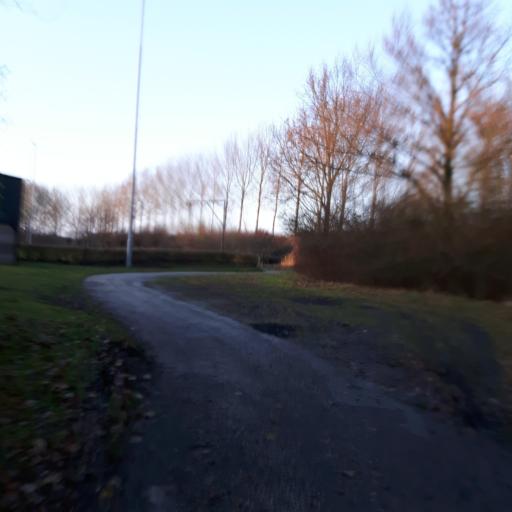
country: NL
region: Zeeland
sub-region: Gemeente Goes
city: Goes
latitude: 51.5195
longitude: 3.8883
